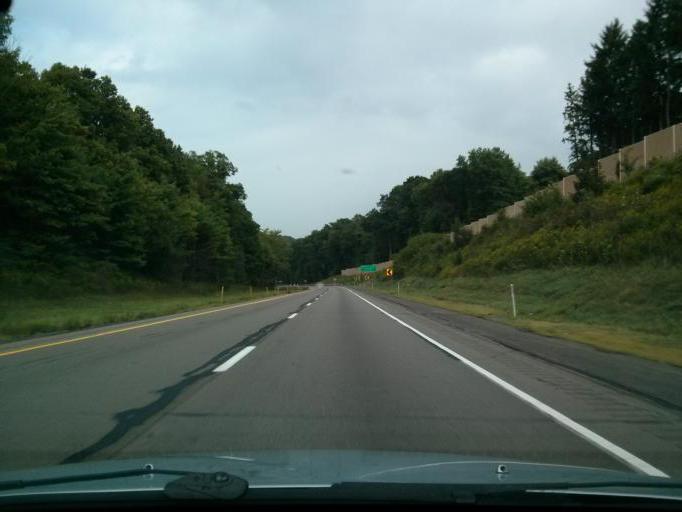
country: US
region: Pennsylvania
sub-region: Jefferson County
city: Brookville
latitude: 41.1691
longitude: -79.0803
